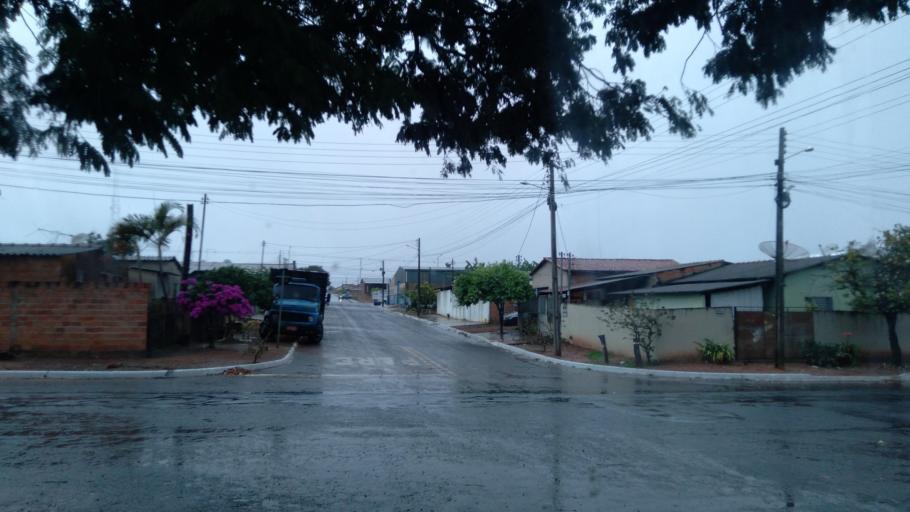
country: BR
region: Goias
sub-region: Mineiros
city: Mineiros
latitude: -17.5430
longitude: -52.5427
